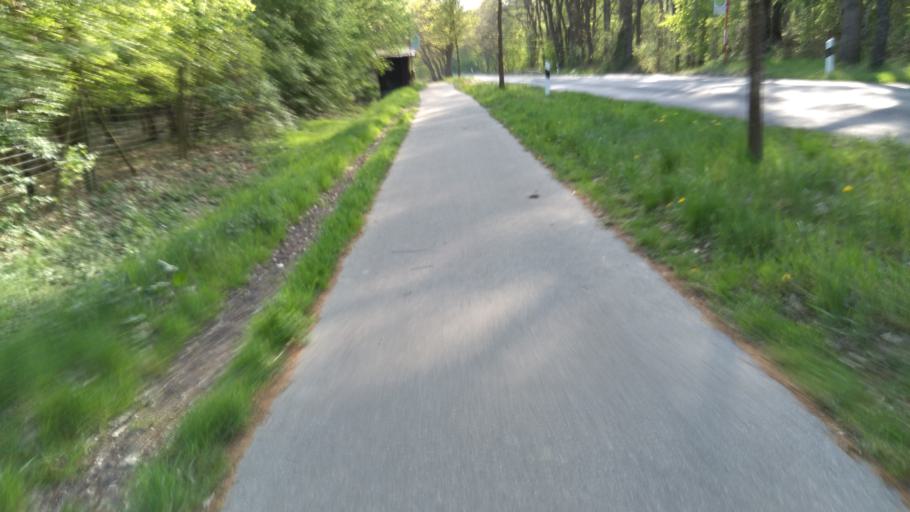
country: DE
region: Lower Saxony
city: Buxtehude
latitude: 53.4397
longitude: 9.6610
